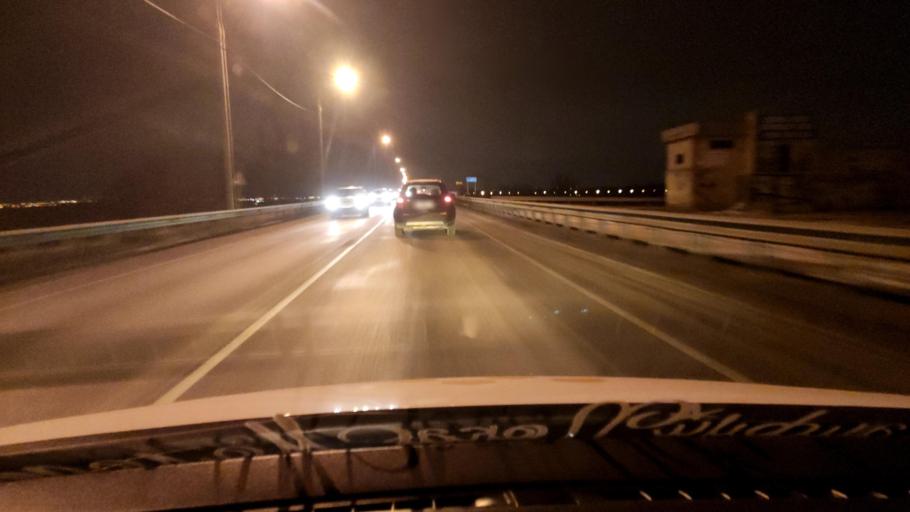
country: RU
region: Voronezj
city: Pridonskoy
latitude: 51.7248
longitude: 39.0582
